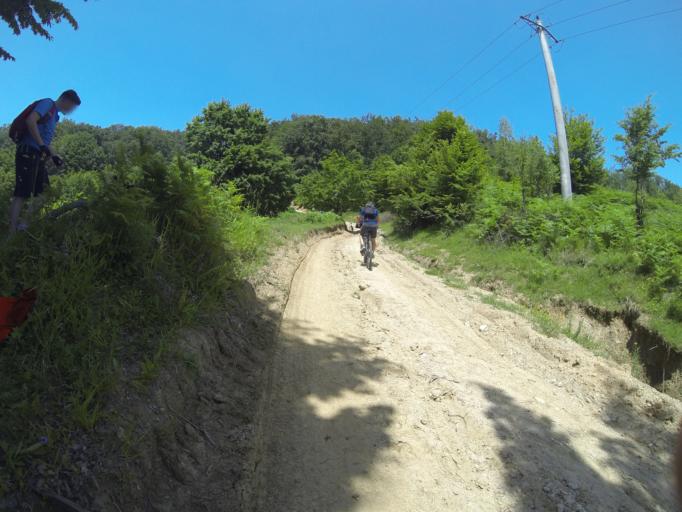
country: RO
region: Valcea
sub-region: Oras Baile Olanesti
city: Baile Olanesti
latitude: 45.2075
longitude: 24.2090
